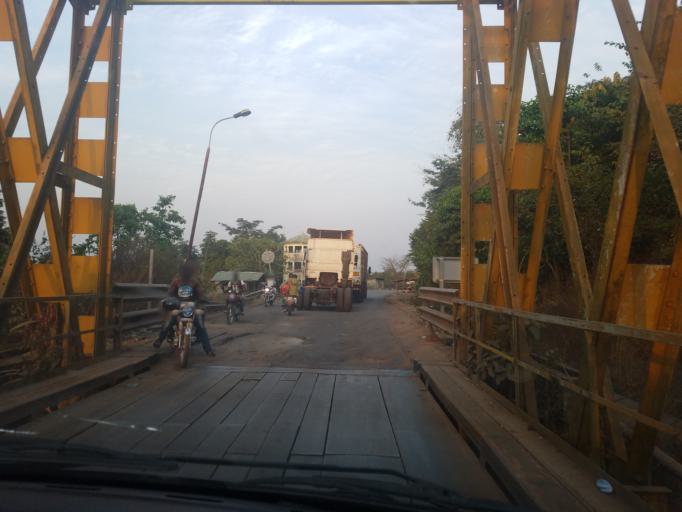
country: GN
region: Boke
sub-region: Fria
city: Fria
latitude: 10.0856
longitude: -13.6774
